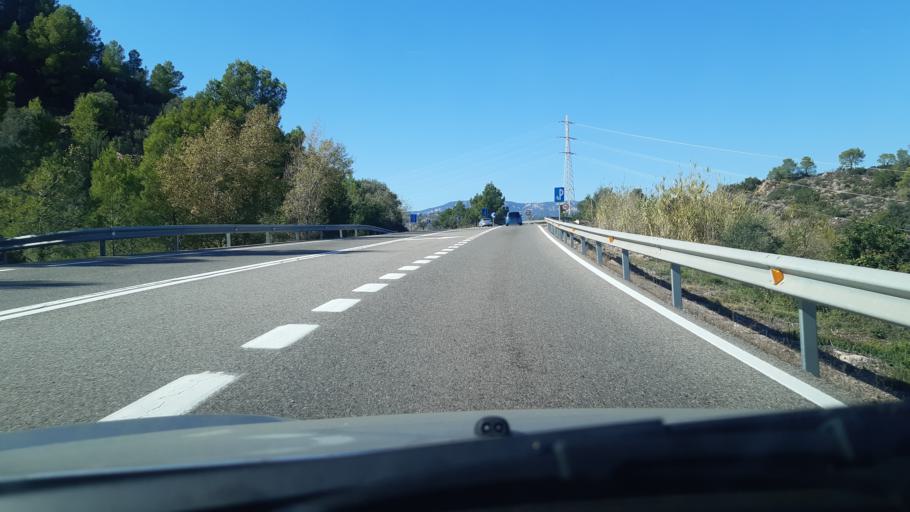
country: ES
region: Catalonia
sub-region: Provincia de Tarragona
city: Benifallet
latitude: 40.9938
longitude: 0.5508
